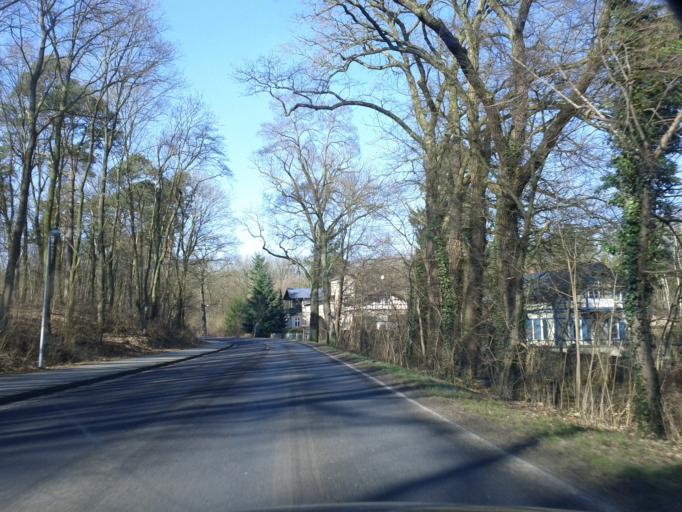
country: DE
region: Brandenburg
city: Spreenhagen
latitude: 52.3997
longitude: 13.9166
